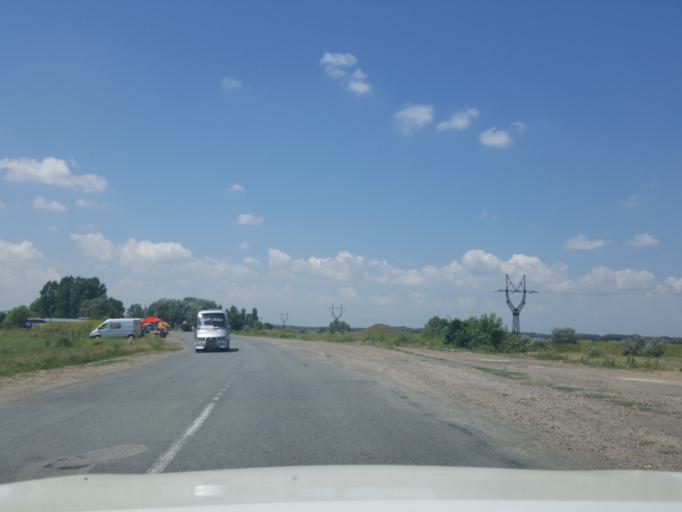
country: UA
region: Odessa
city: Bilyayivka
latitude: 46.4116
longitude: 30.1273
